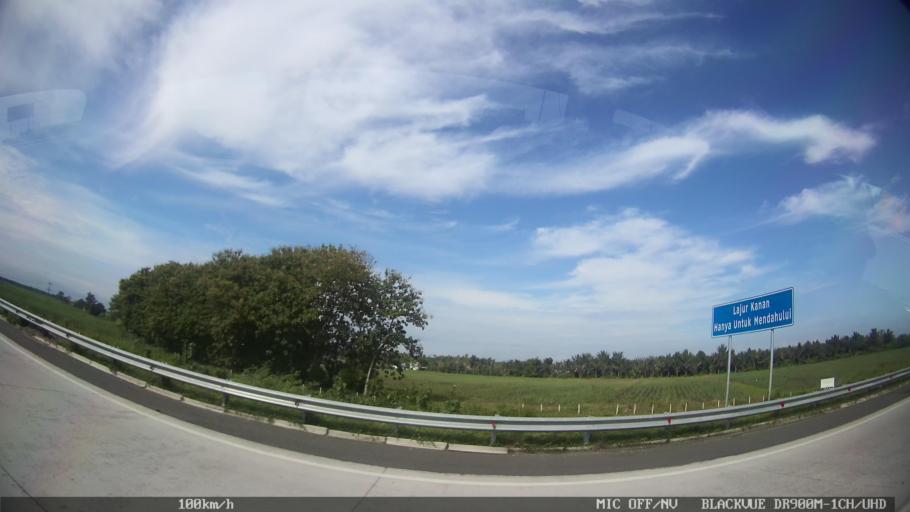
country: ID
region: North Sumatra
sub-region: Kabupaten Langkat
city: Stabat
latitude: 3.7015
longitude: 98.5395
